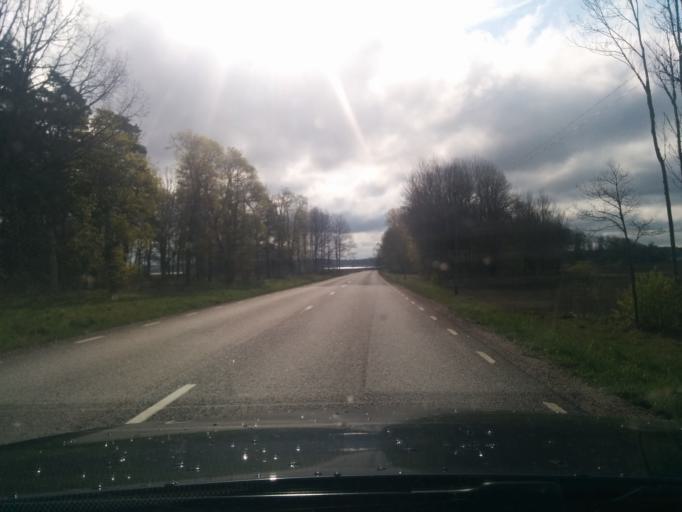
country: SE
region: Uppsala
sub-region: Tierps Kommun
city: Orbyhus
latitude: 60.1764
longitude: 17.6253
